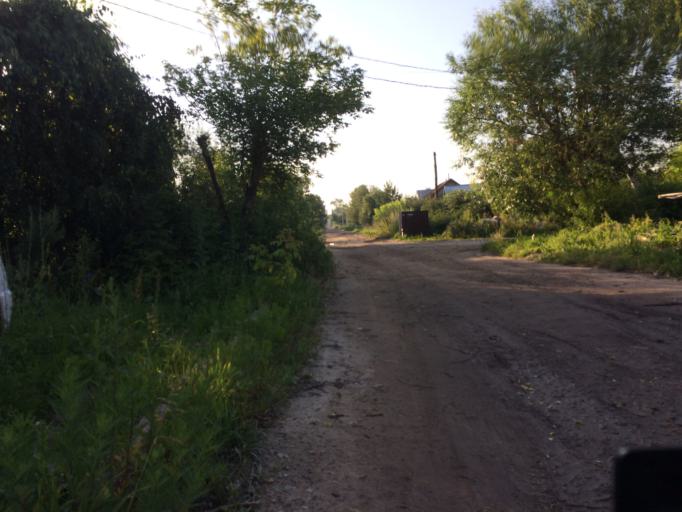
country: RU
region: Mariy-El
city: Yoshkar-Ola
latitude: 56.6543
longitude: 47.8875
